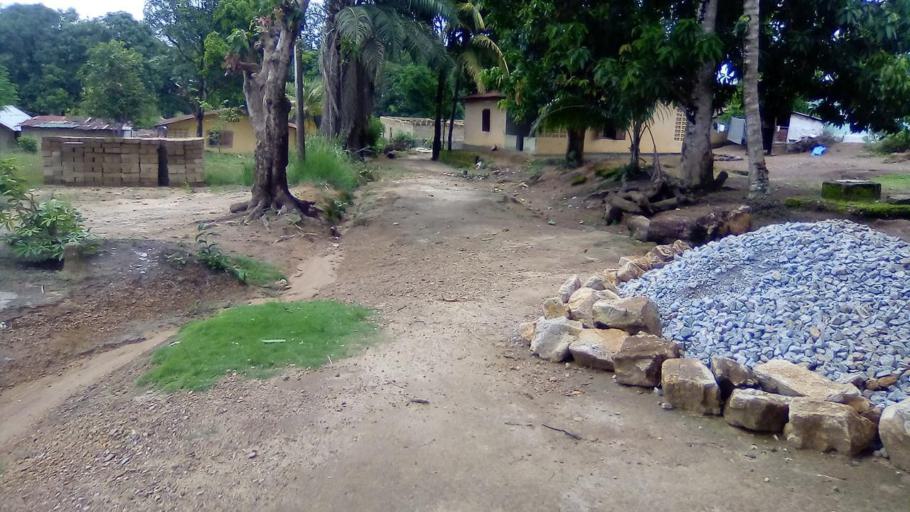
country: SL
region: Southern Province
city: Bo
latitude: 7.9496
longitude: -11.7508
